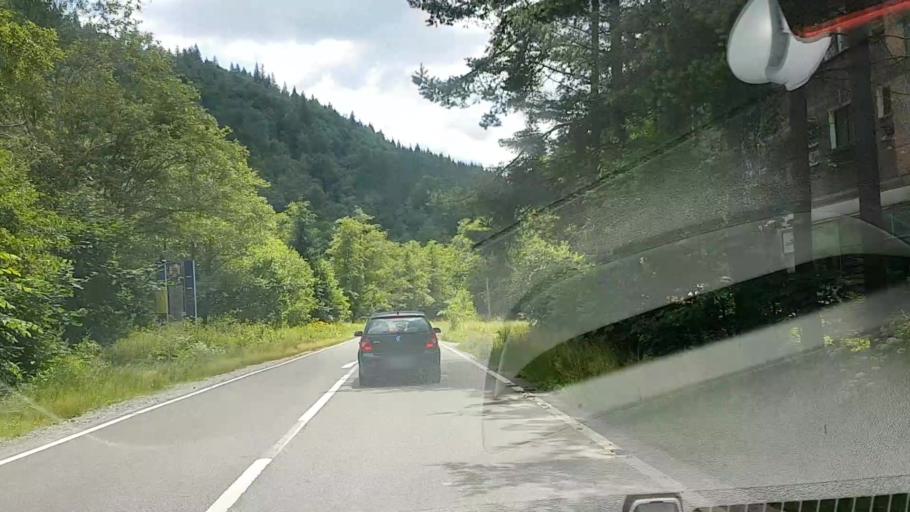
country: RO
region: Suceava
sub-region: Comuna Crucea
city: Crucea
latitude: 47.2996
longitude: 25.6314
